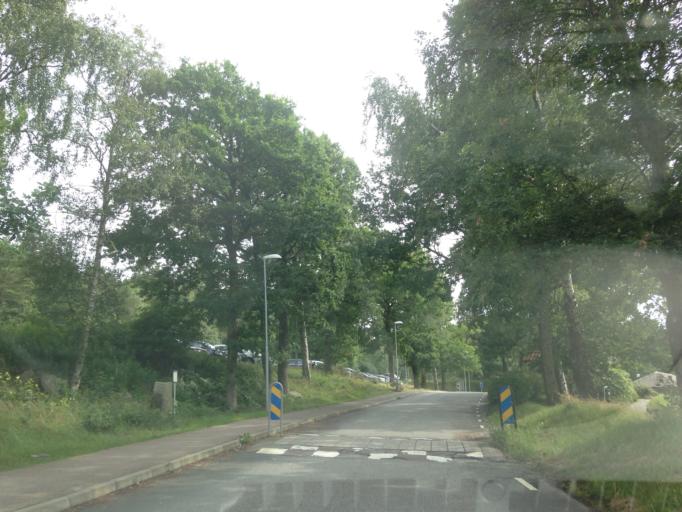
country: SE
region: Vaestra Goetaland
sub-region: Goteborg
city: Goeteborg
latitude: 57.7788
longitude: 11.9562
